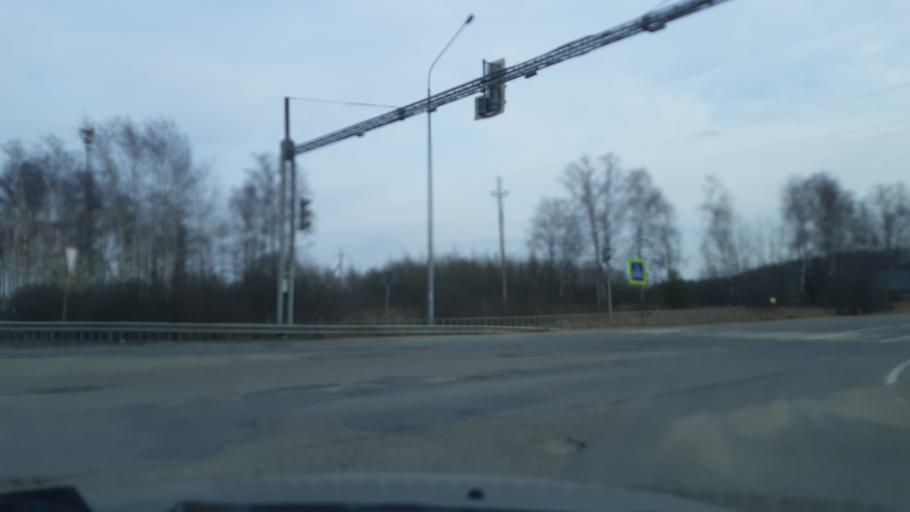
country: RU
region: Vladimir
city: Luknovo
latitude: 56.2383
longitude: 42.0339
